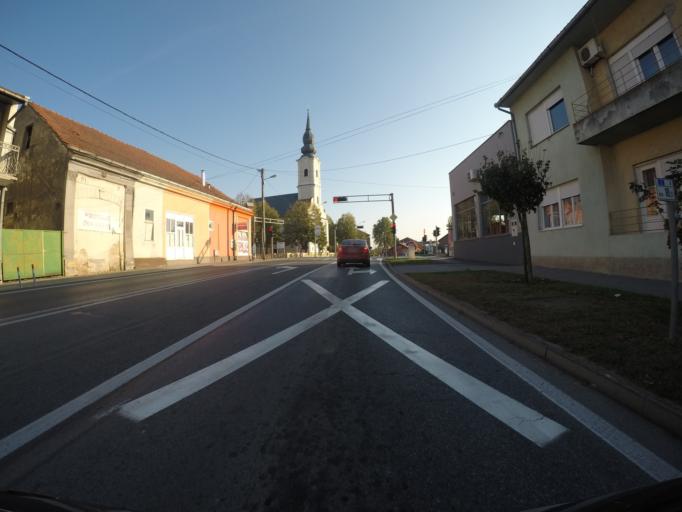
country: HR
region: Virovitick-Podravska
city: Pitomaca
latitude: 45.9532
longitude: 17.2328
